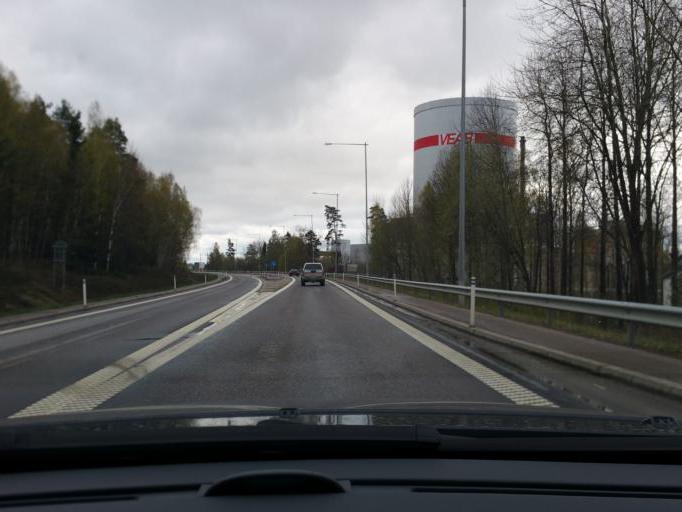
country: SE
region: Kronoberg
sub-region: Vaxjo Kommun
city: Vaexjoe
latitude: 56.8707
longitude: 14.8383
